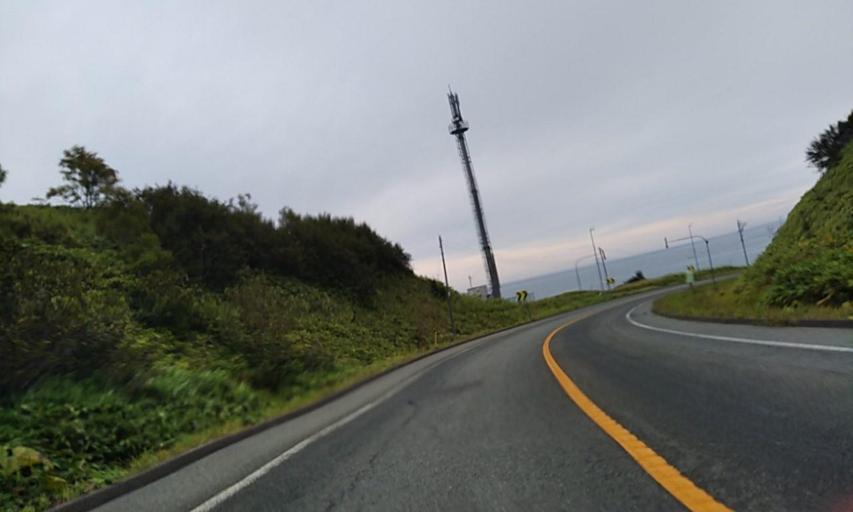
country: JP
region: Hokkaido
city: Makubetsu
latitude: 45.4257
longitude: 142.0280
